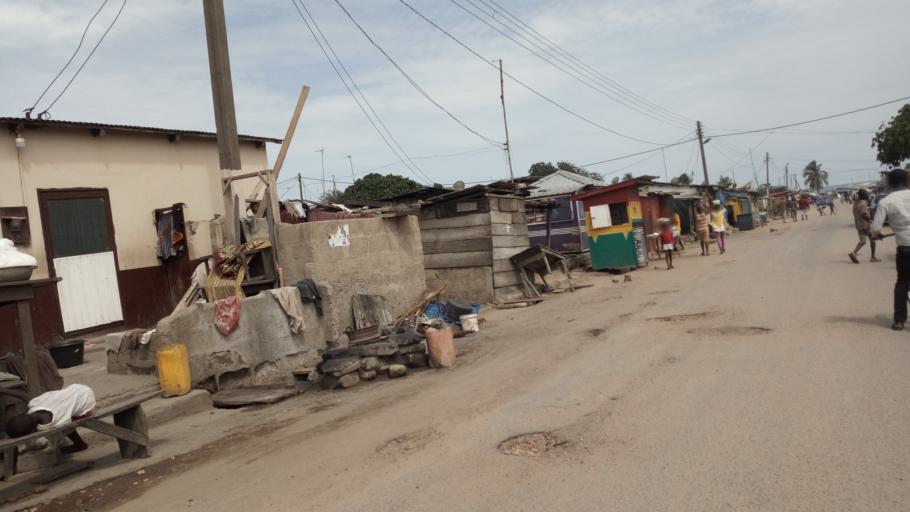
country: GH
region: Central
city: Winneba
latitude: 5.3447
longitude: -0.6184
